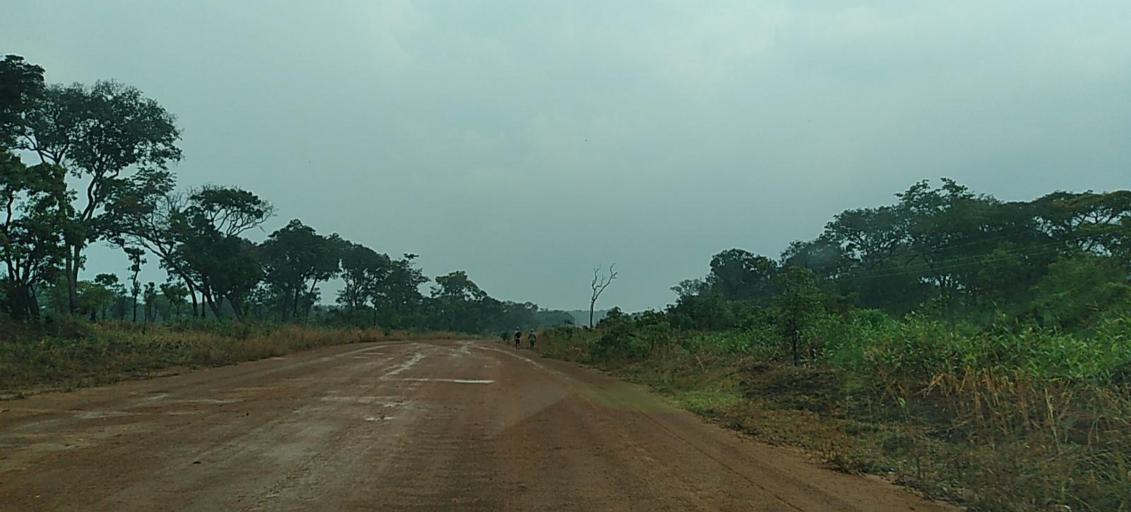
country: ZM
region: North-Western
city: Mwinilunga
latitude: -11.5905
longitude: 24.3876
